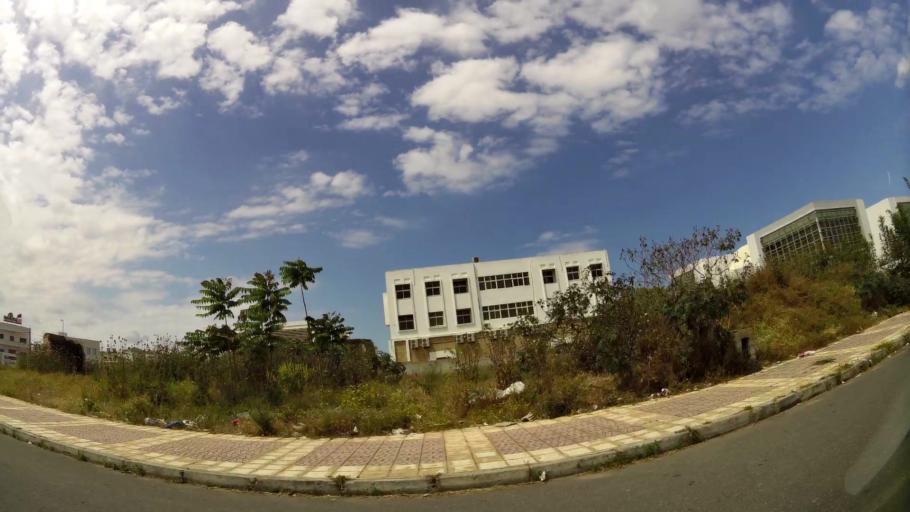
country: MA
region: Gharb-Chrarda-Beni Hssen
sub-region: Kenitra Province
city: Kenitra
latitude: 34.2524
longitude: -6.5988
